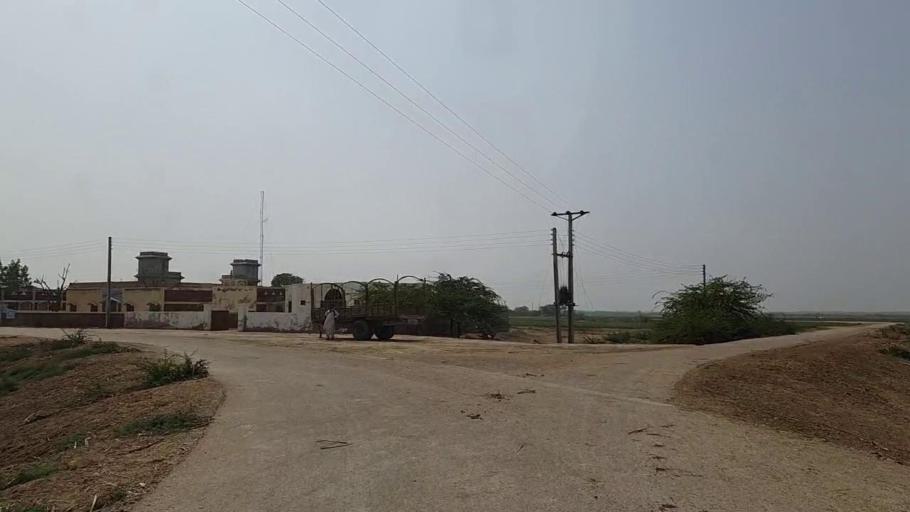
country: PK
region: Sindh
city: Naukot
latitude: 24.7983
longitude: 69.3337
